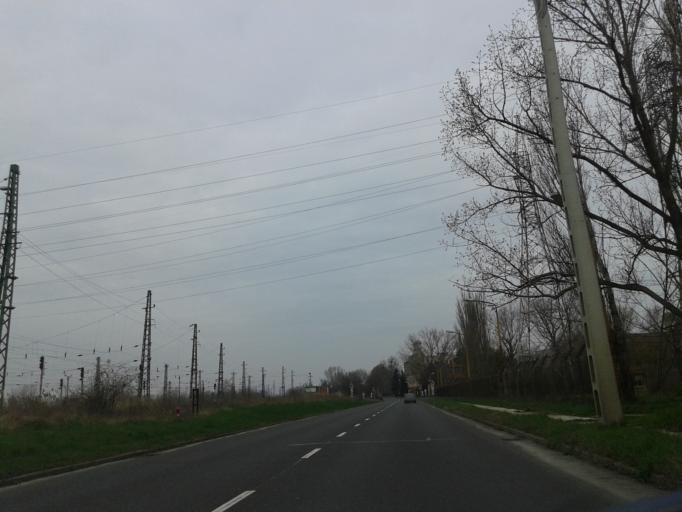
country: HU
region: Komarom-Esztergom
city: Almasfuzito
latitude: 47.7277
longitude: 18.2558
